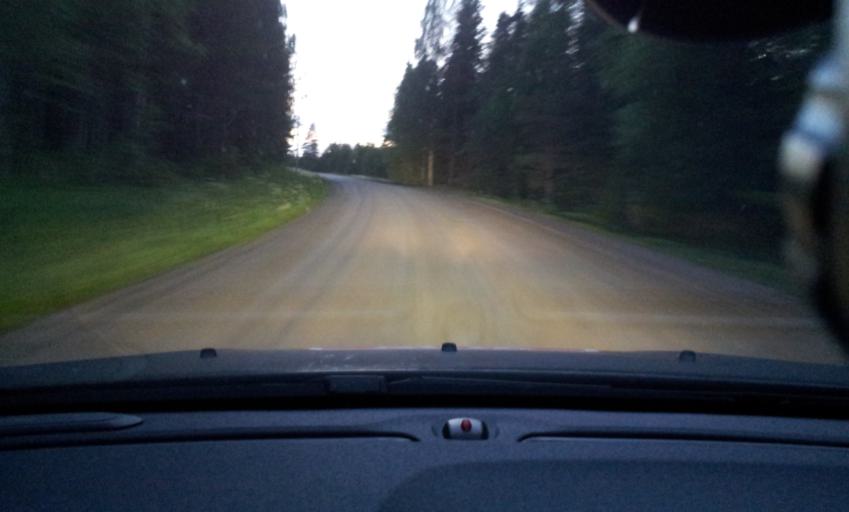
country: SE
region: Jaemtland
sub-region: Braecke Kommun
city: Braecke
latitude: 62.7382
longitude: 15.4552
